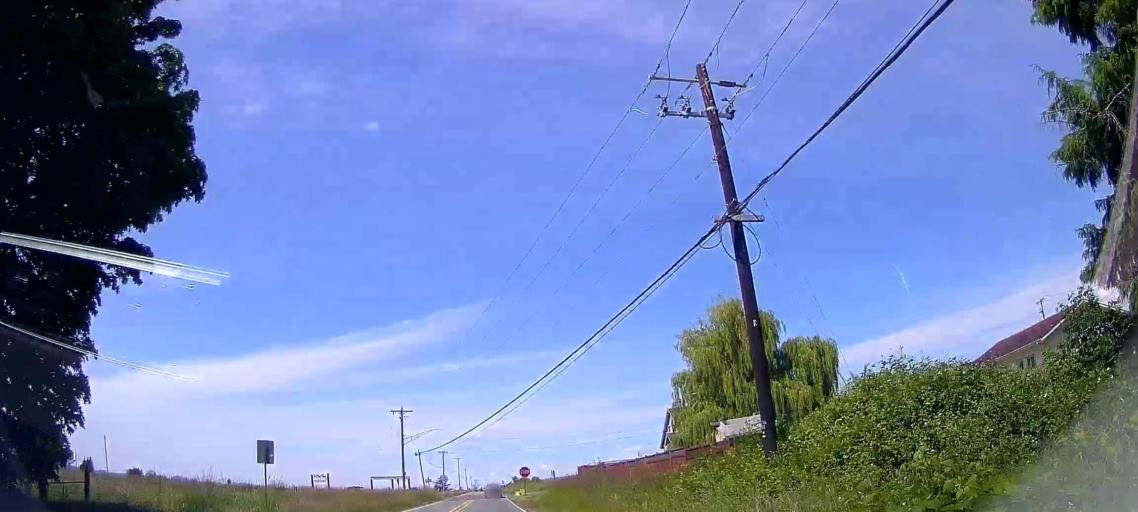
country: US
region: Washington
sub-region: Snohomish County
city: Stanwood
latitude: 48.2678
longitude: -122.3610
